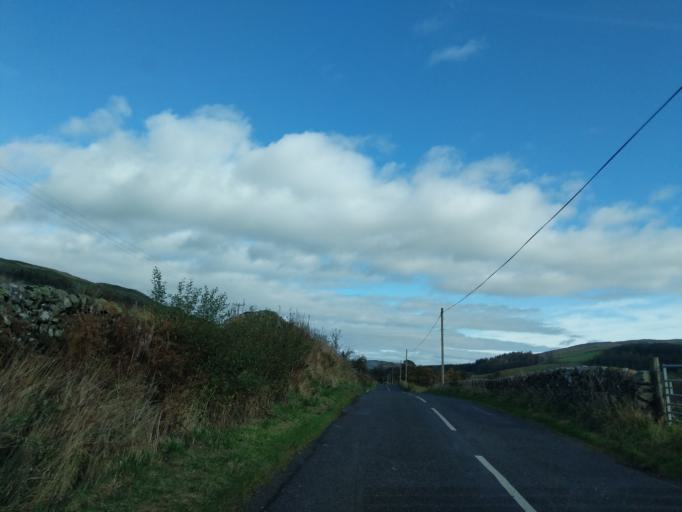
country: GB
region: Scotland
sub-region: Dumfries and Galloway
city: Sanquhar
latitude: 55.1652
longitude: -3.9693
